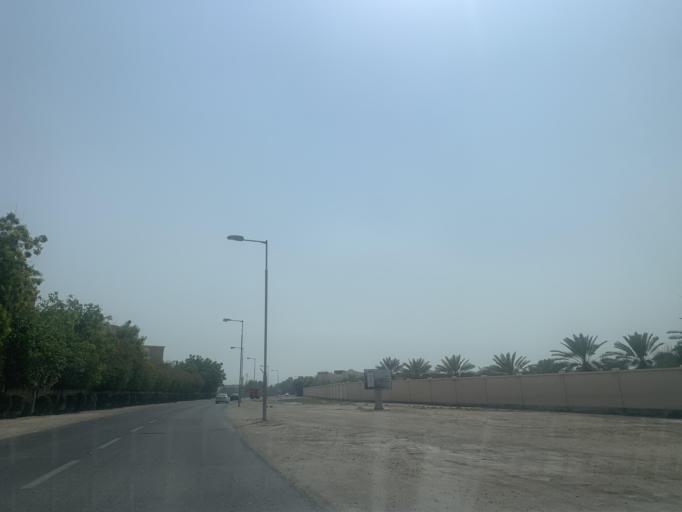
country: BH
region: Central Governorate
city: Madinat Hamad
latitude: 26.1691
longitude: 50.4574
